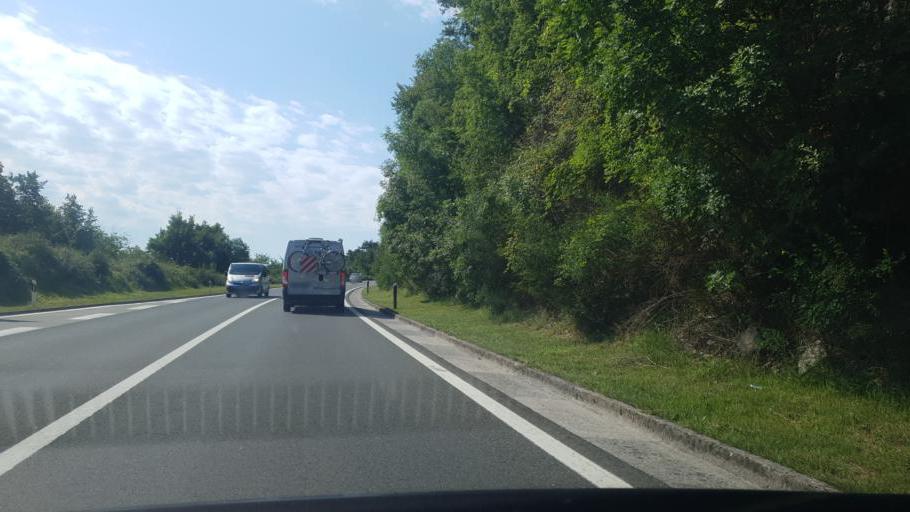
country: HR
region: Primorsko-Goranska
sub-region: Grad Opatija
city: Opatija
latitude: 45.3349
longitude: 14.2878
